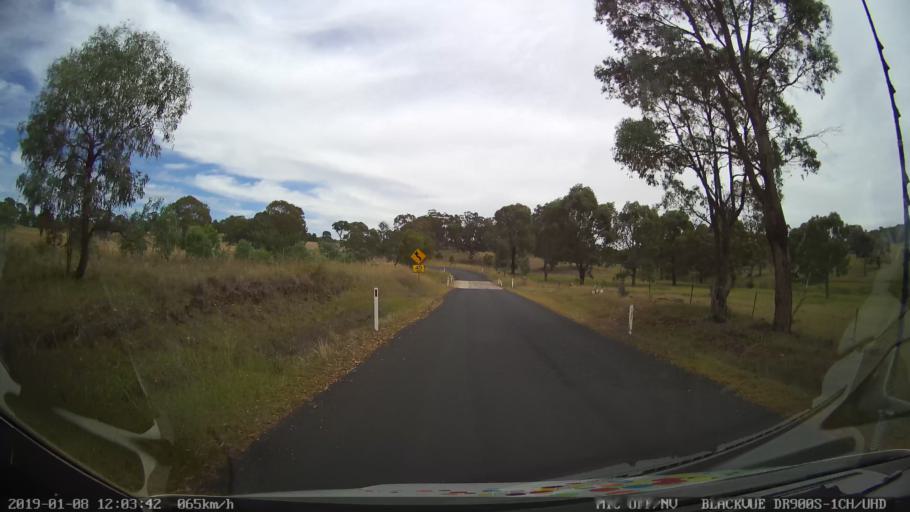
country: AU
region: New South Wales
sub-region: Armidale Dumaresq
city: Armidale
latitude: -30.4485
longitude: 151.5919
